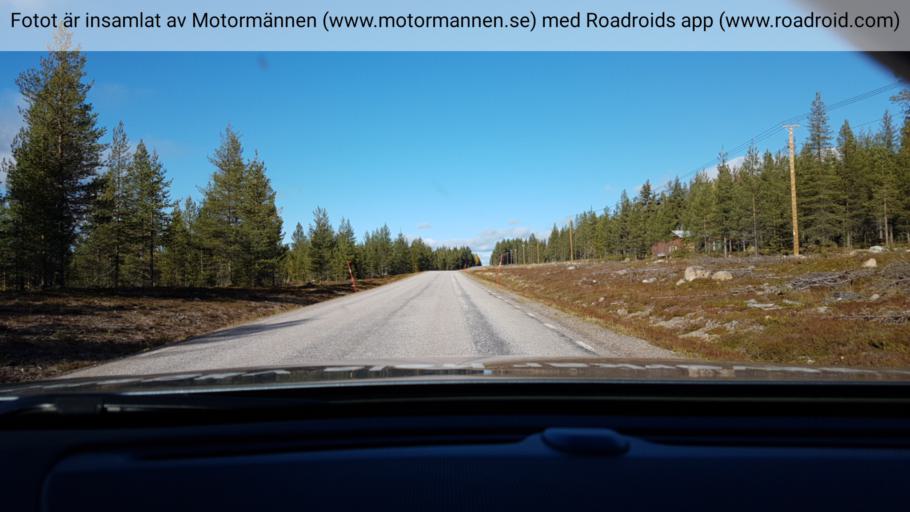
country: SE
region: Vaesterbotten
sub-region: Mala Kommun
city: Mala
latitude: 65.7820
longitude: 18.5020
